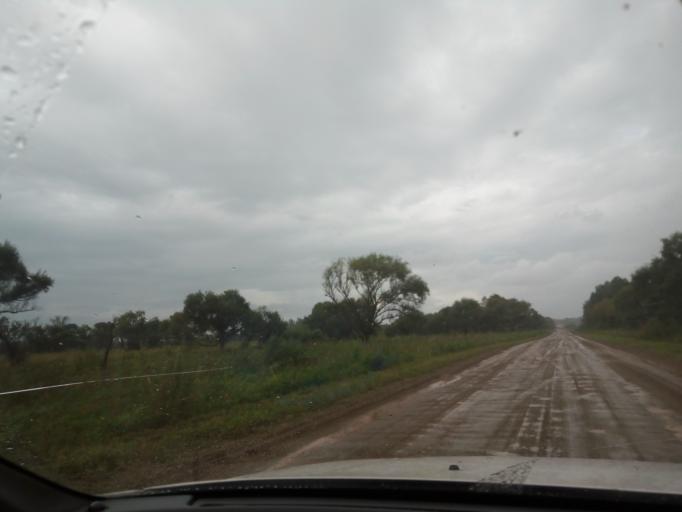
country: RU
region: Primorskiy
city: Lazo
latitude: 45.8467
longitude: 133.6450
